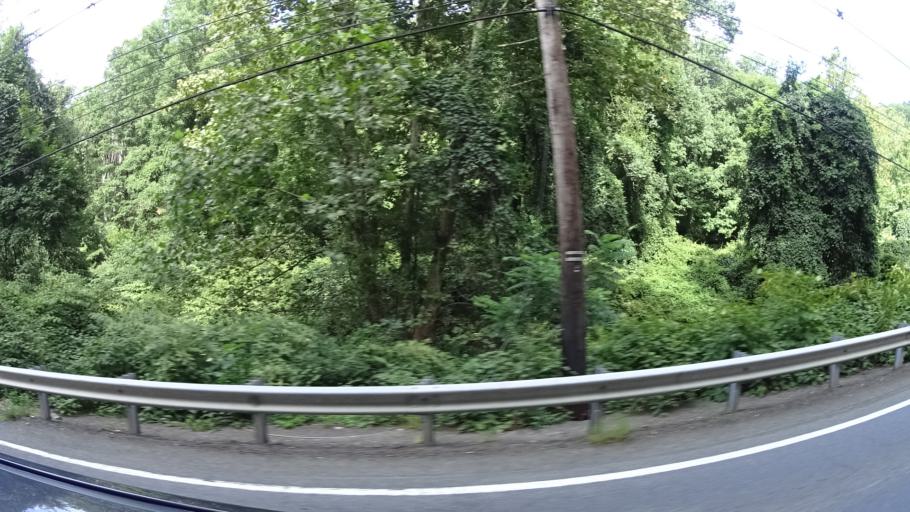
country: US
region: New Jersey
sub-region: Union County
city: Scotch Plains
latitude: 40.6654
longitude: -74.4033
